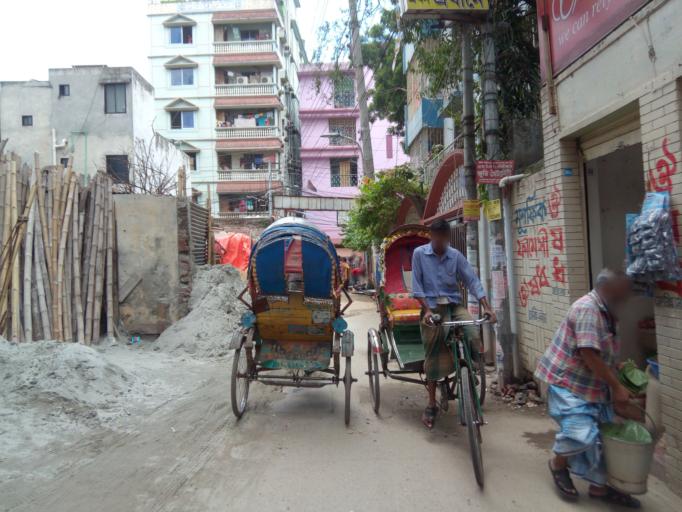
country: BD
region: Dhaka
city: Azimpur
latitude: 23.7440
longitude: 90.3885
